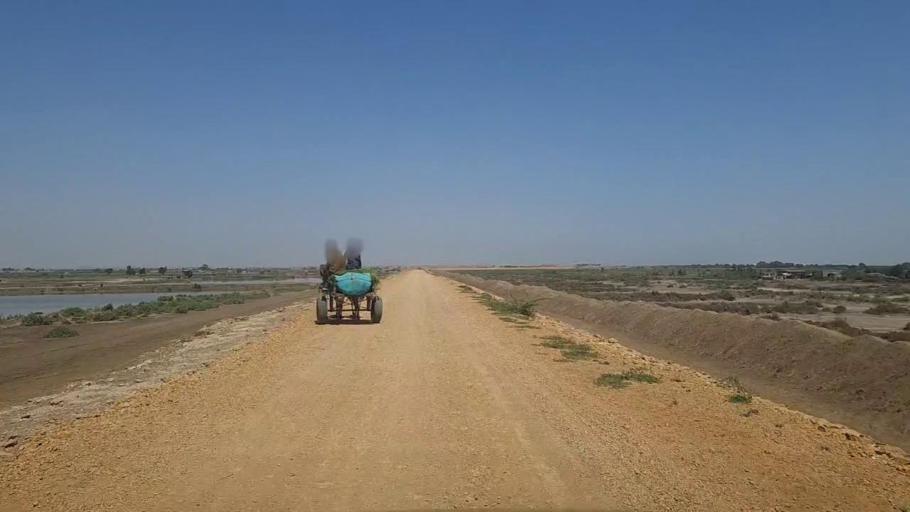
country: PK
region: Sindh
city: Thatta
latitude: 24.7896
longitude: 67.9971
